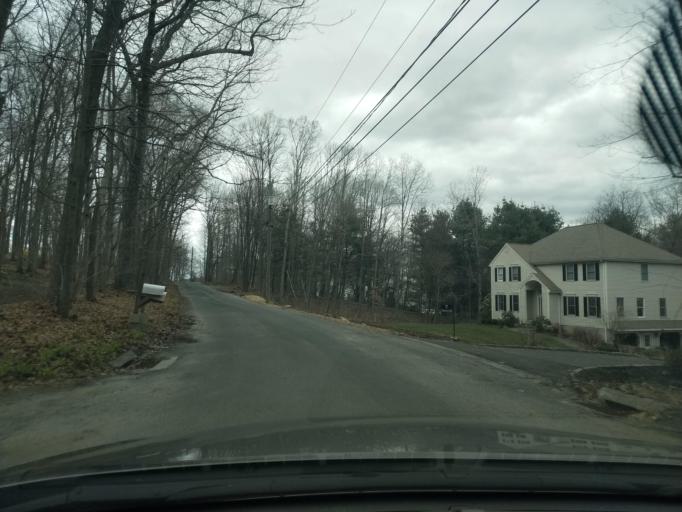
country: US
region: Connecticut
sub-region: Fairfield County
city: Newtown
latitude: 41.3638
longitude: -73.2730
